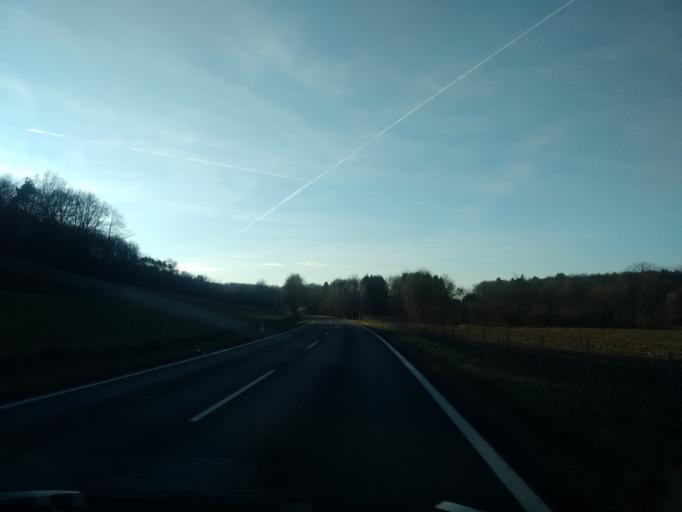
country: AT
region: Lower Austria
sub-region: Politischer Bezirk Sankt Polten
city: Neulengbach
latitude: 48.1835
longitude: 15.8653
